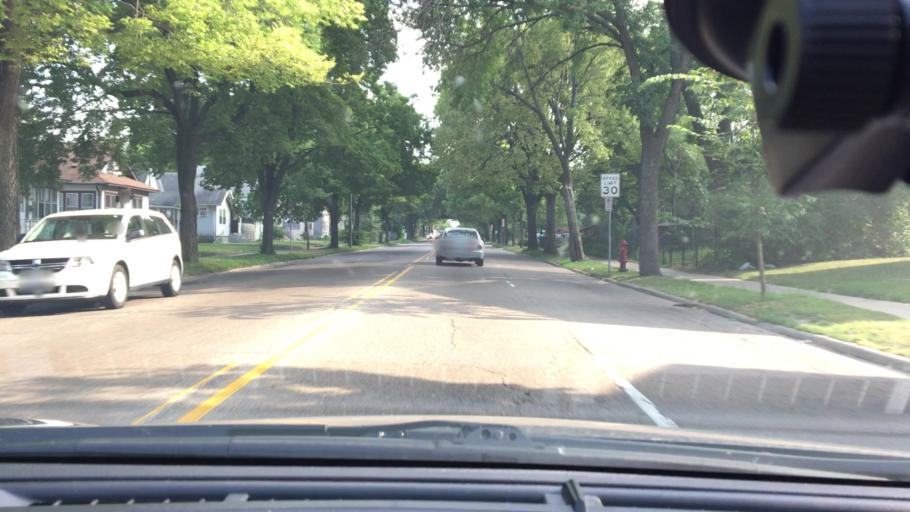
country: US
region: Minnesota
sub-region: Hennepin County
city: Minneapolis
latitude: 44.9549
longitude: -93.2474
